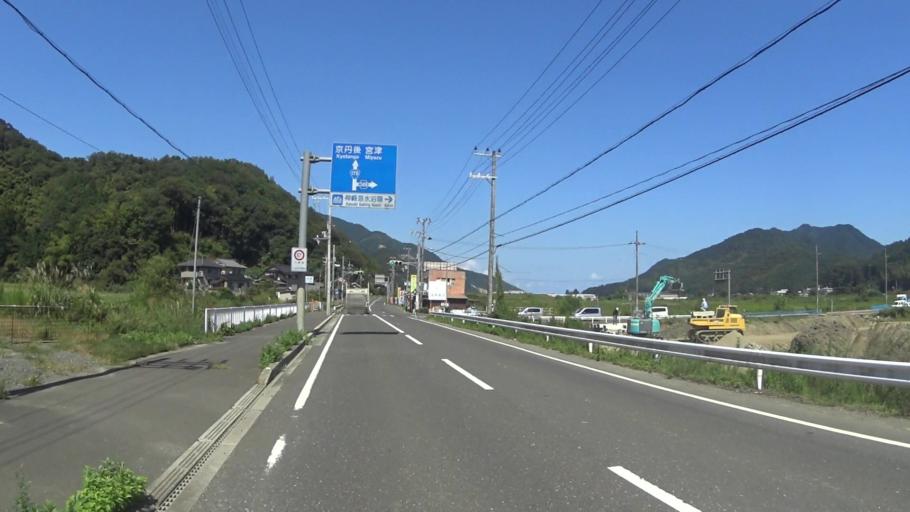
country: JP
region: Kyoto
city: Maizuru
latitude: 35.4651
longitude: 135.2784
